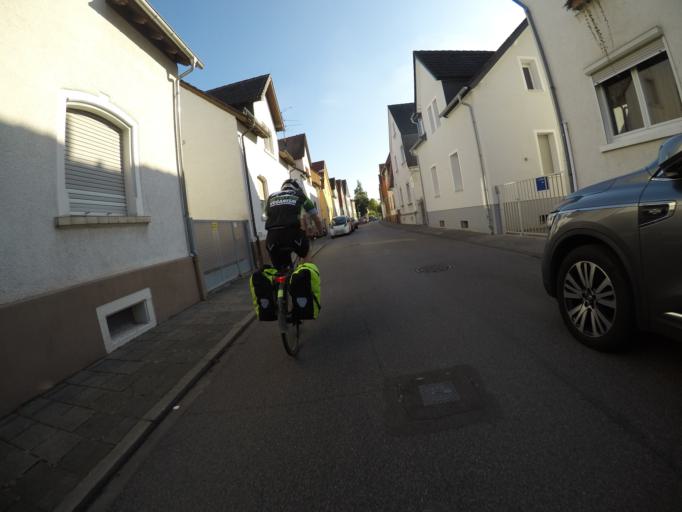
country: DE
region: Hesse
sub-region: Regierungsbezirk Darmstadt
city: Darmstadt
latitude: 49.9073
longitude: 8.6555
